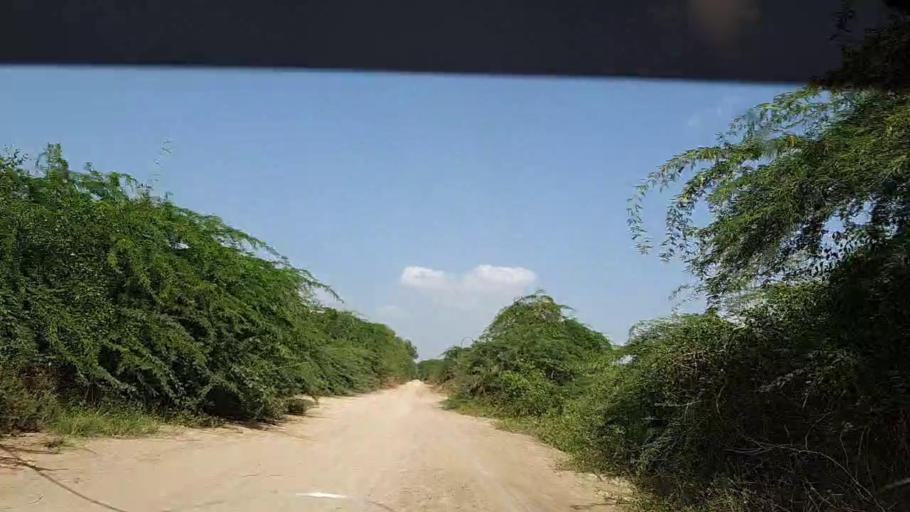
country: PK
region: Sindh
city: Badin
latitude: 24.5875
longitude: 68.7935
